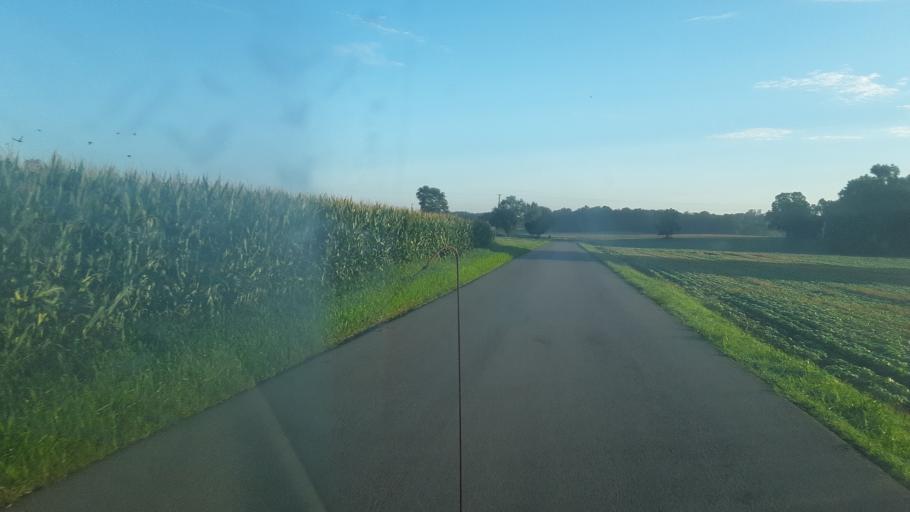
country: US
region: Kentucky
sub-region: Todd County
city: Guthrie
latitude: 36.7049
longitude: -87.1702
